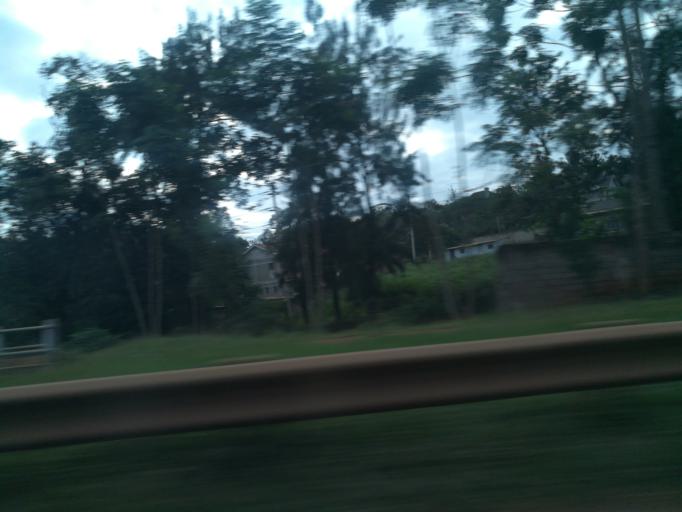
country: KE
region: Nairobi Area
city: Thika
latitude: -1.0268
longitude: 37.0652
